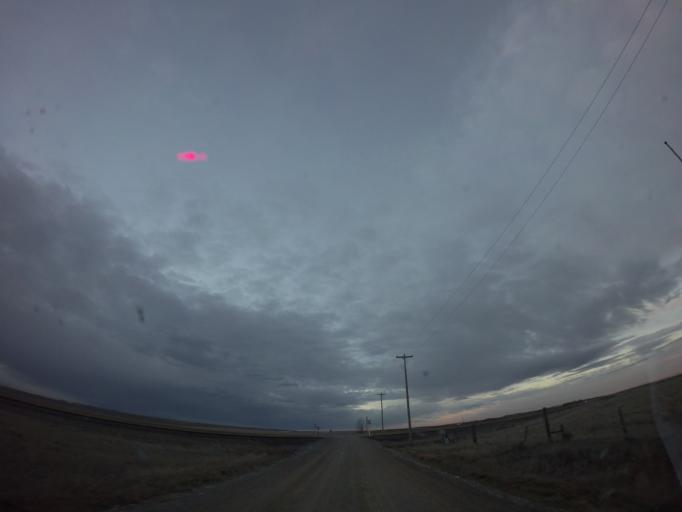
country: US
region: Montana
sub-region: Yellowstone County
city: Billings
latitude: 45.9436
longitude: -108.7076
